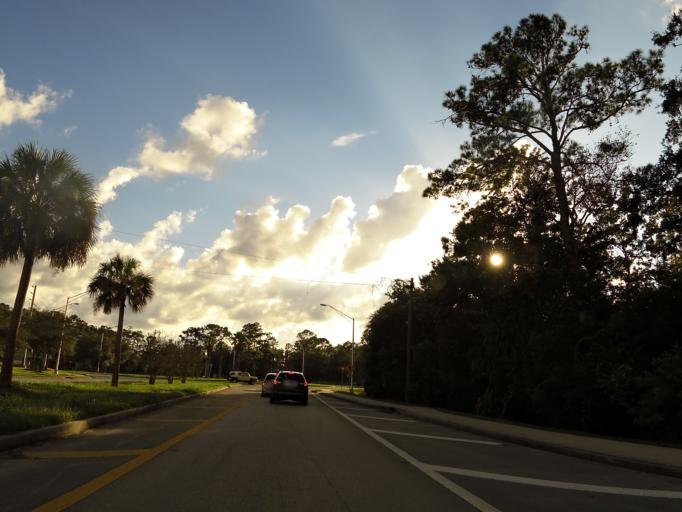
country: US
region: Florida
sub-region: Saint Johns County
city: Palm Valley
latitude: 30.1519
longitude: -81.3761
